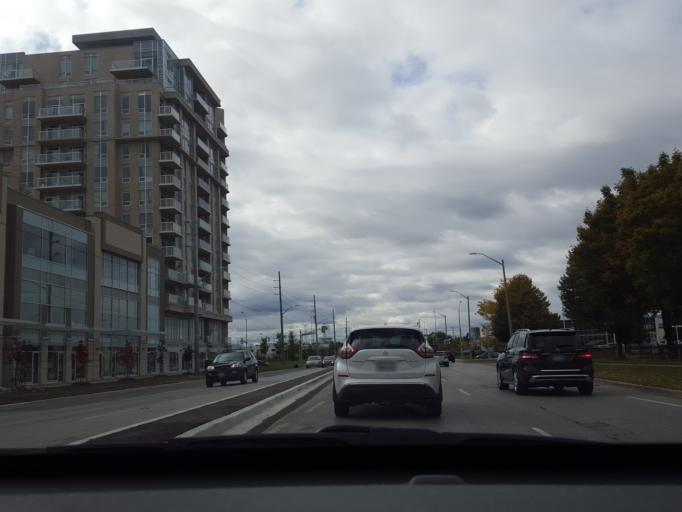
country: CA
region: Ontario
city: Markham
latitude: 43.8571
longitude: -79.3043
